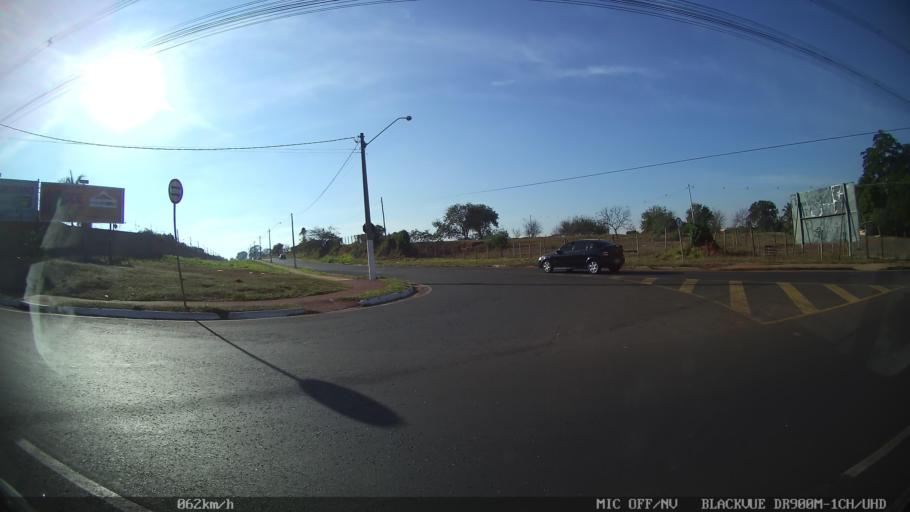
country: BR
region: Sao Paulo
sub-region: Sao Jose Do Rio Preto
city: Sao Jose do Rio Preto
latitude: -20.7838
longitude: -49.3430
